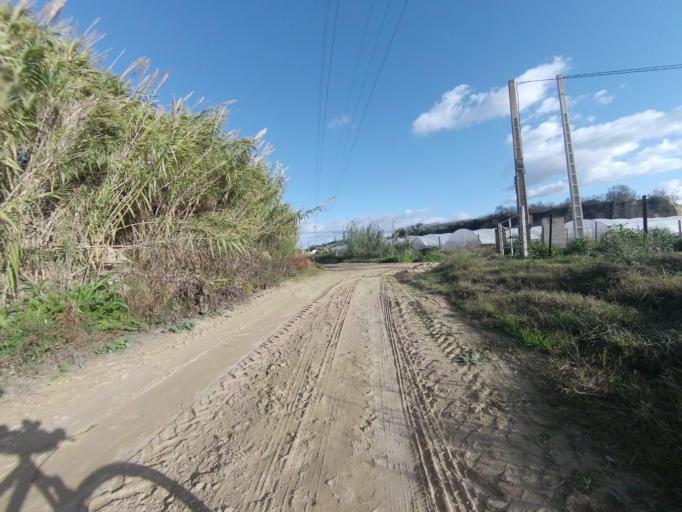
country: ES
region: Andalusia
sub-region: Provincia de Huelva
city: Moguer
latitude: 37.2655
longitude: -6.8554
